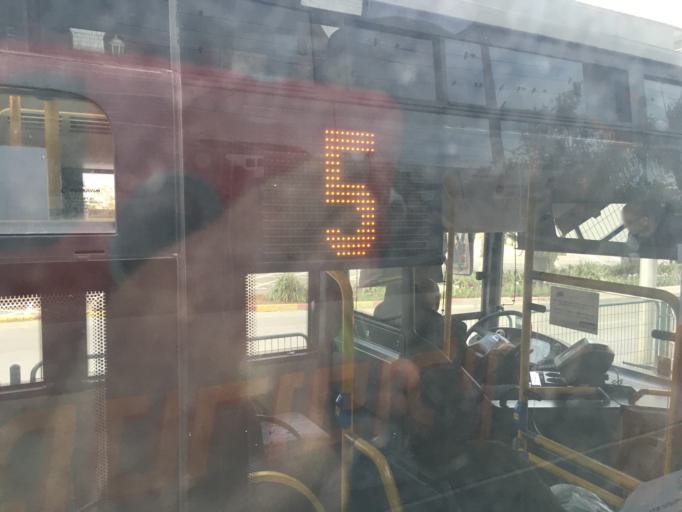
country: IL
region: Central District
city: Kfar Saba
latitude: 32.1763
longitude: 34.9041
